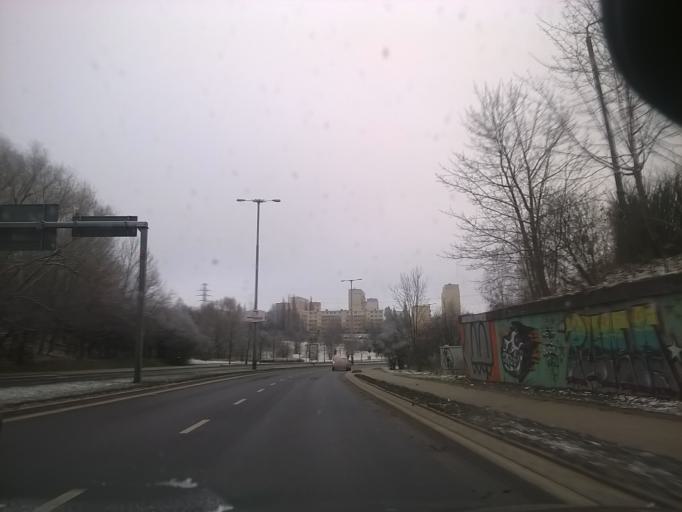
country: PL
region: Warmian-Masurian Voivodeship
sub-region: Powiat olsztynski
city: Olsztyn
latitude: 53.7606
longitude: 20.5000
